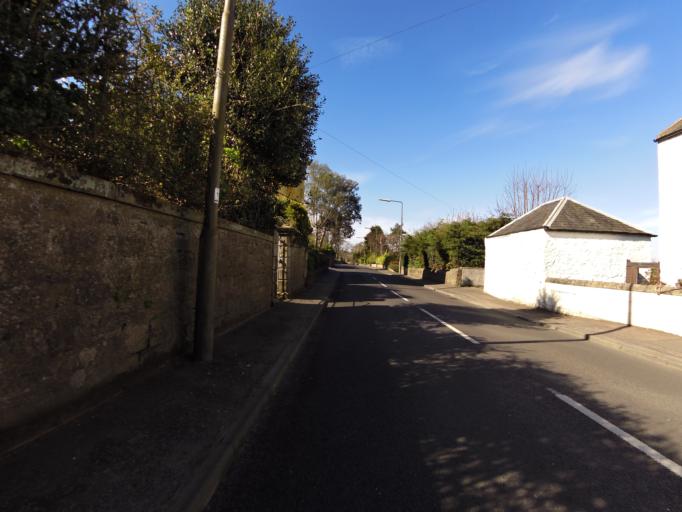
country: GB
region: Scotland
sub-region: Fife
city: Newport-On-Tay
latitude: 56.4336
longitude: -2.9534
